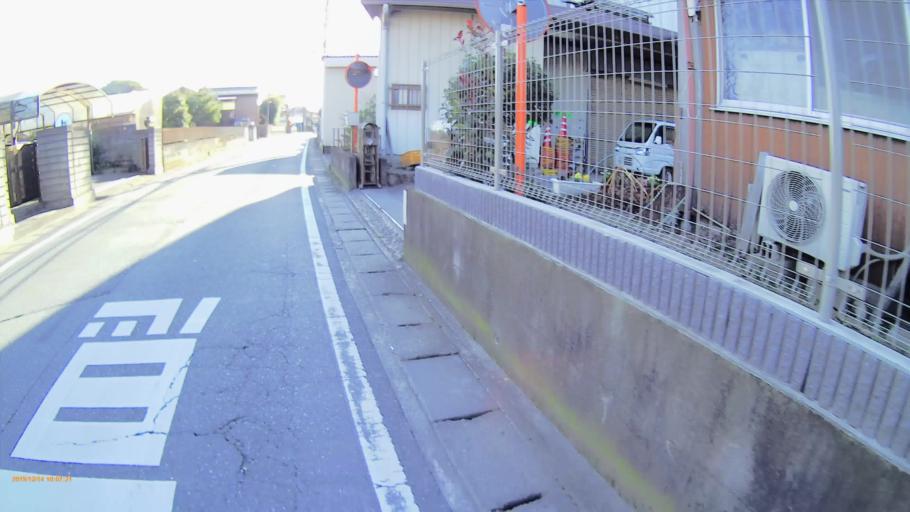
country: JP
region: Saitama
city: Kumagaya
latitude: 36.1749
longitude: 139.3442
